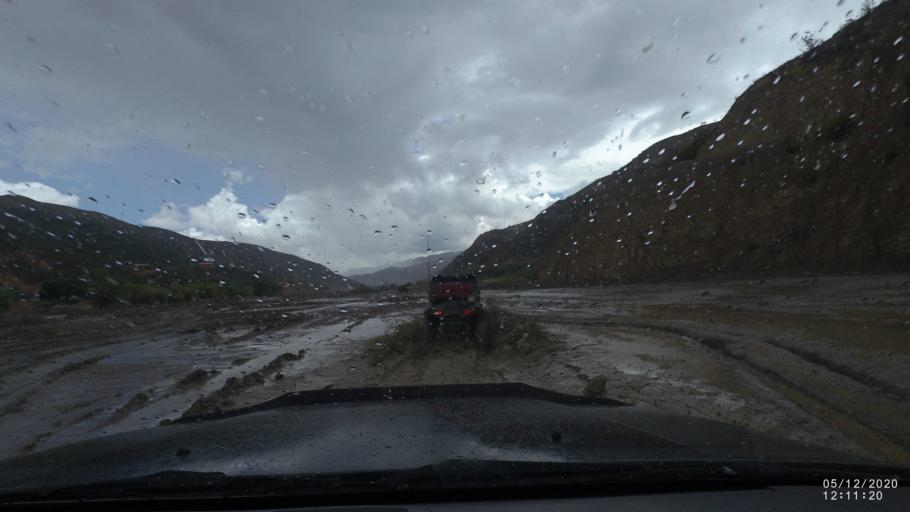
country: BO
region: Cochabamba
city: Sipe Sipe
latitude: -17.5658
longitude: -66.3733
